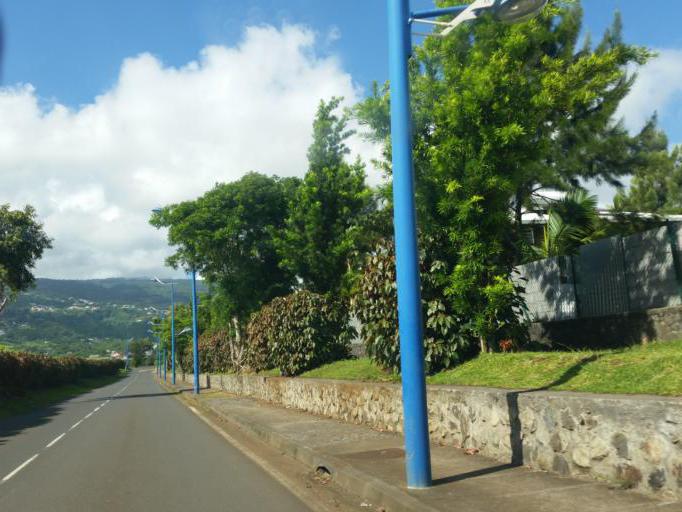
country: RE
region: Reunion
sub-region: Reunion
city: Sainte-Marie
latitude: -20.9229
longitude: 55.5312
